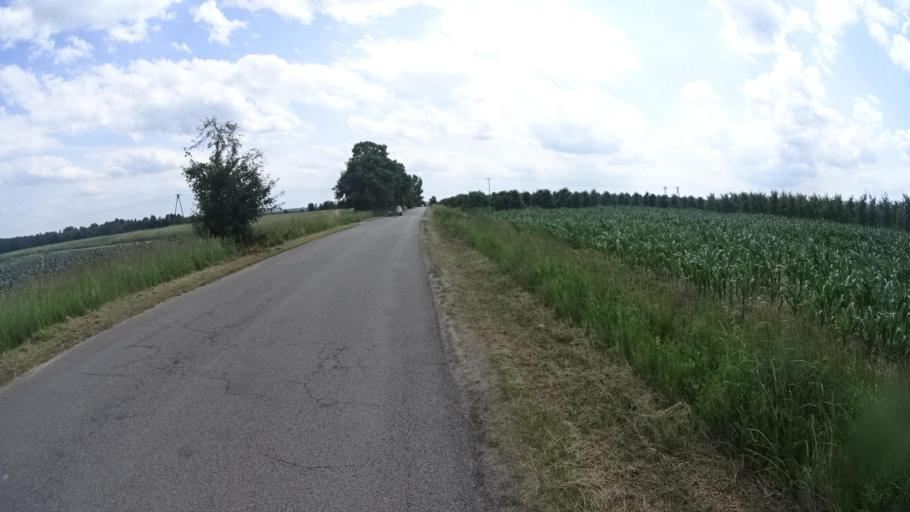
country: PL
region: Masovian Voivodeship
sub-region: Powiat bialobrzeski
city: Wysmierzyce
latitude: 51.6663
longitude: 20.8312
